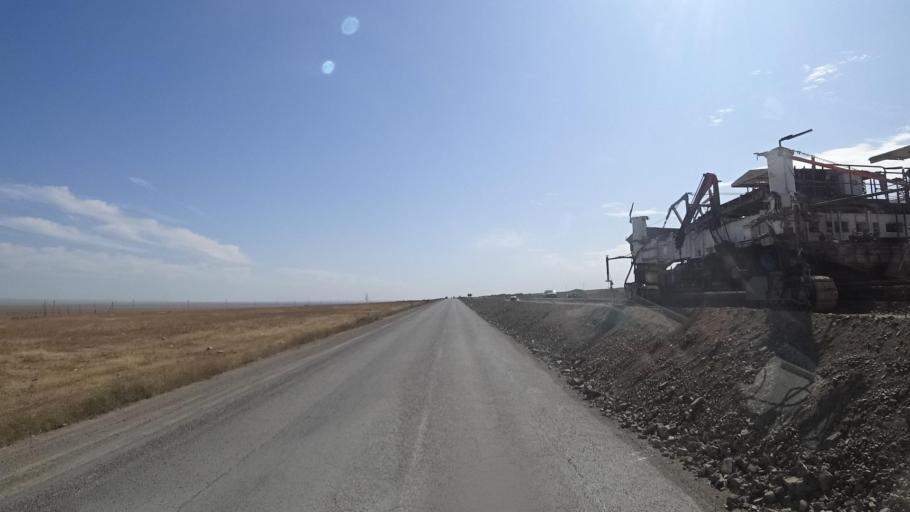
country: KG
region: Chuy
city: Ivanovka
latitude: 43.3843
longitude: 75.1749
